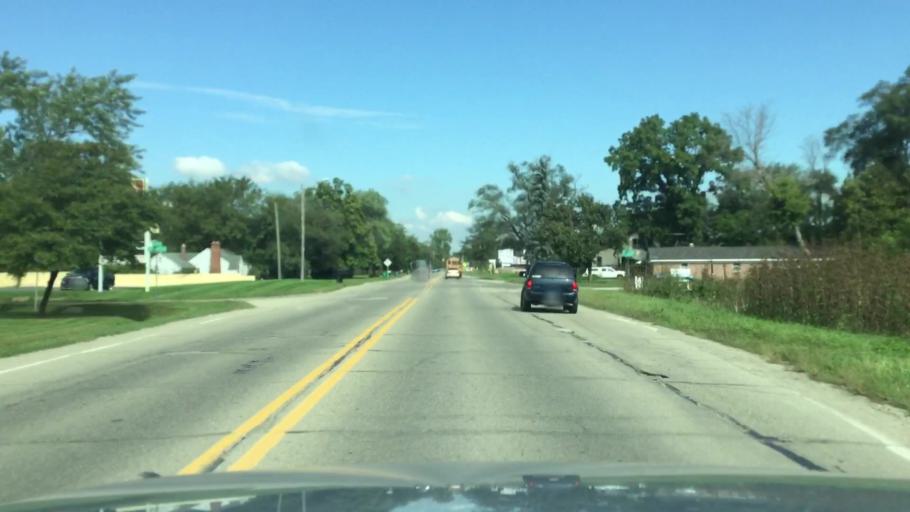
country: US
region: Michigan
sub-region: Wayne County
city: Belleville
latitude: 42.1928
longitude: -83.4840
